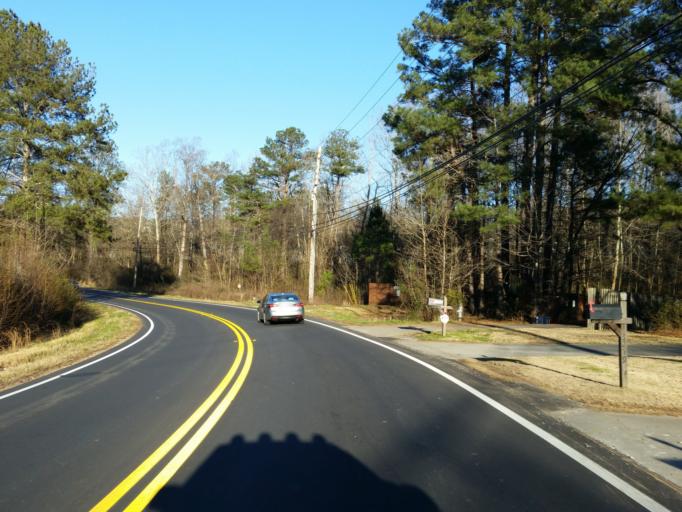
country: US
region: Georgia
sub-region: Cherokee County
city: Woodstock
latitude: 34.0928
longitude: -84.4761
